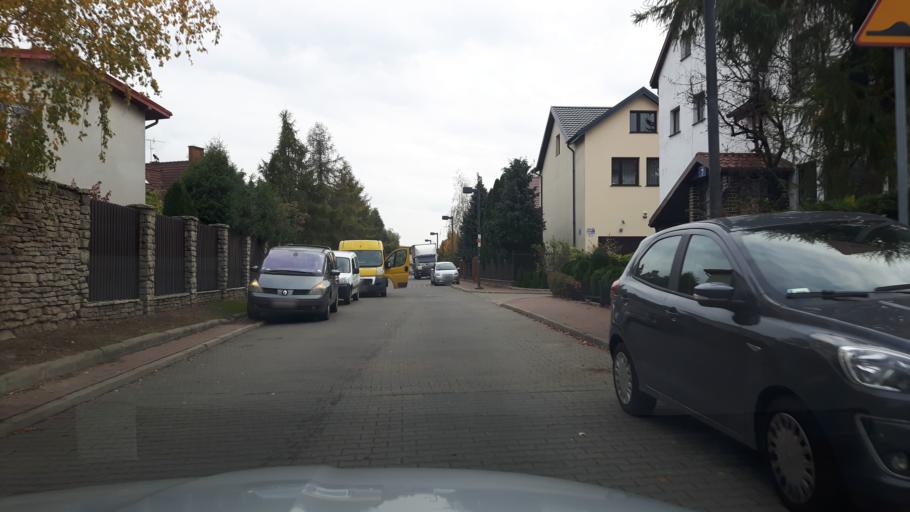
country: PL
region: Masovian Voivodeship
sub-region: Warszawa
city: Targowek
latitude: 52.2854
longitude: 21.0579
